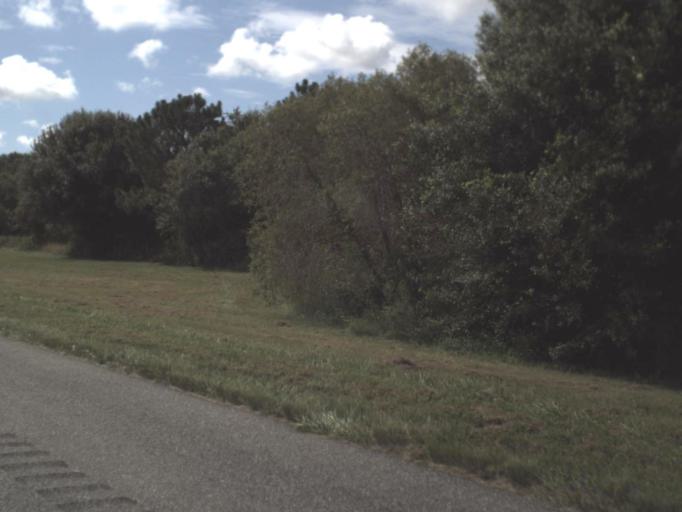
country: US
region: Florida
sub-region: Charlotte County
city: Port Charlotte
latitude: 27.0808
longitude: -82.1086
